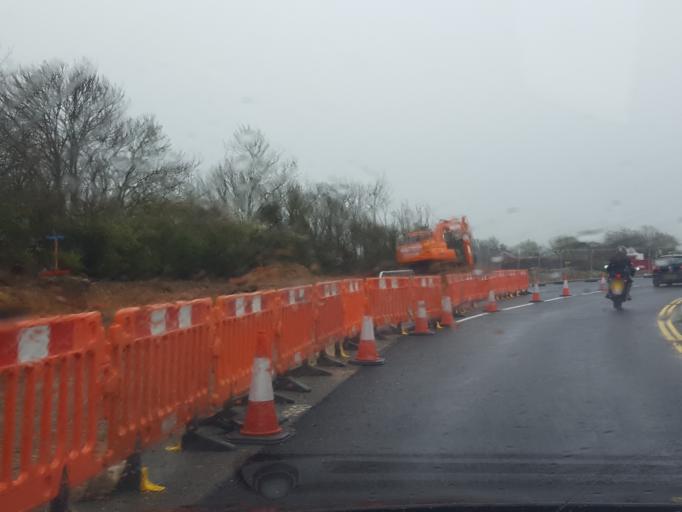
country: GB
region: England
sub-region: Essex
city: Great Horkesley
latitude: 51.9200
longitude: 0.8877
